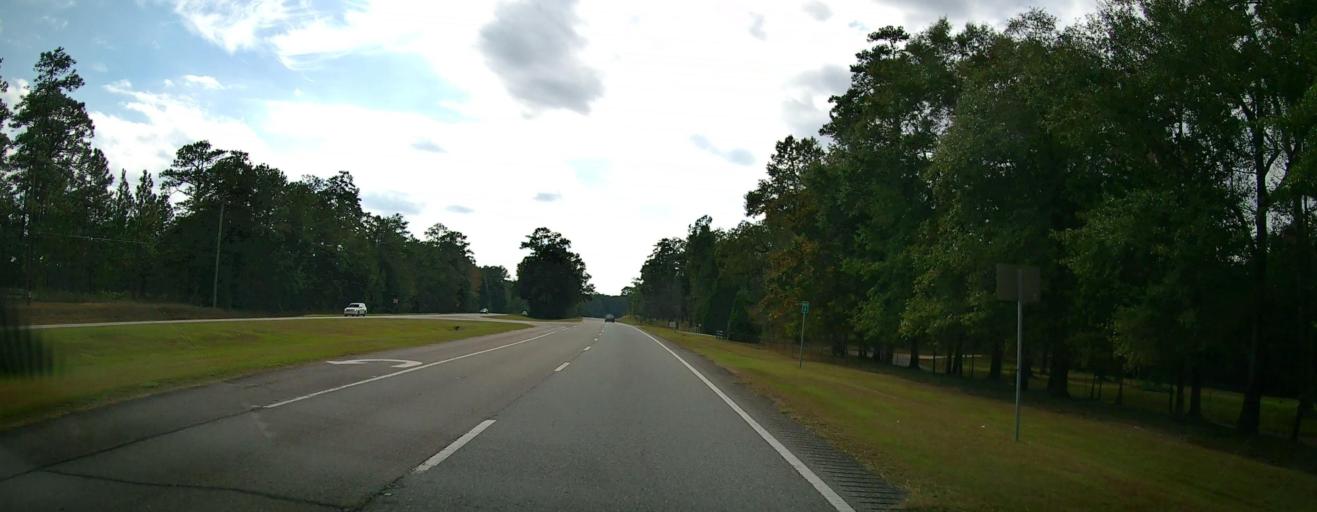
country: US
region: Georgia
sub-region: Thomas County
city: Thomasville
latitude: 30.7765
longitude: -84.0662
